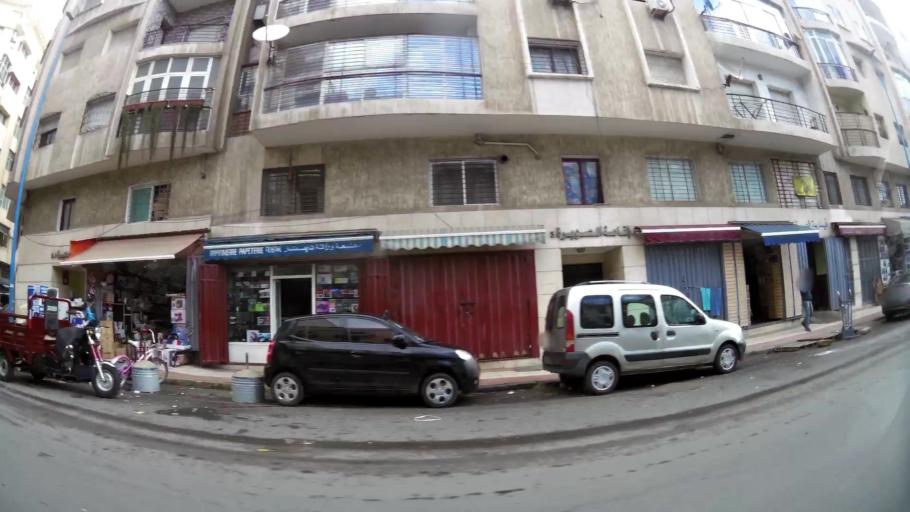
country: MA
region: Grand Casablanca
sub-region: Casablanca
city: Casablanca
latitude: 33.5886
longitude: -7.6065
